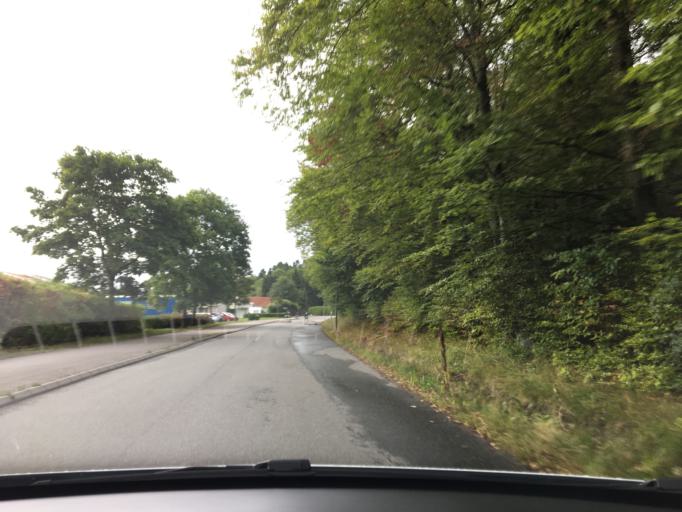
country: SE
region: Vaestra Goetaland
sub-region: Ale Kommun
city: Nodinge-Nol
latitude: 57.8884
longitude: 12.0454
